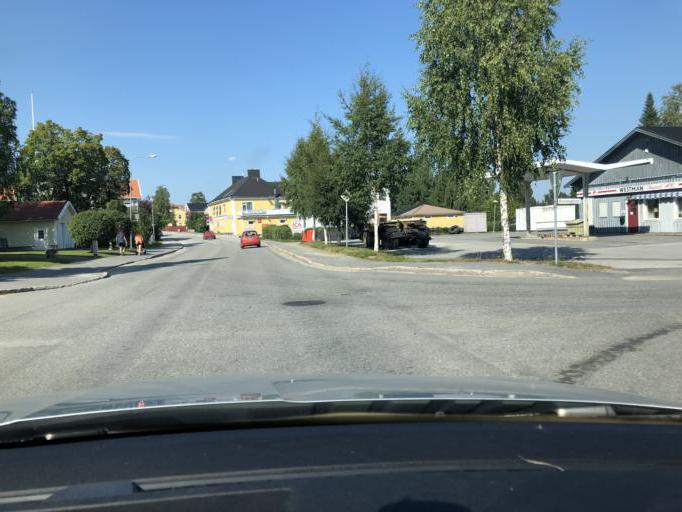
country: SE
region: Vaesternorrland
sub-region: OErnskoeldsviks Kommun
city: Bredbyn
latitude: 63.4470
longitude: 18.1140
